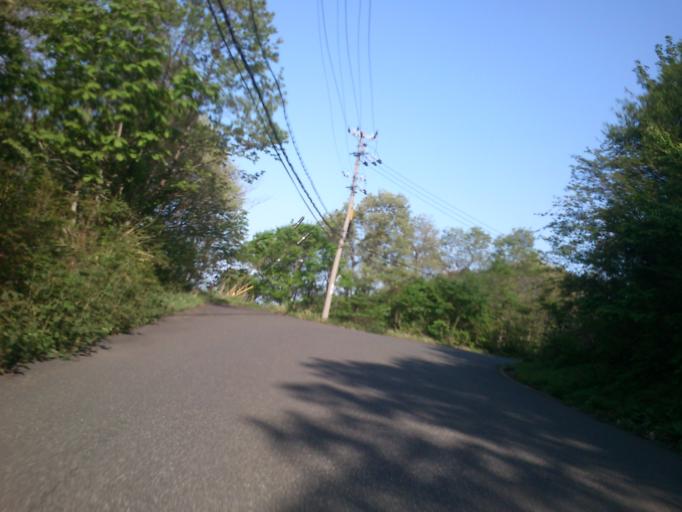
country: JP
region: Kyoto
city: Miyazu
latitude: 35.7078
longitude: 135.1901
